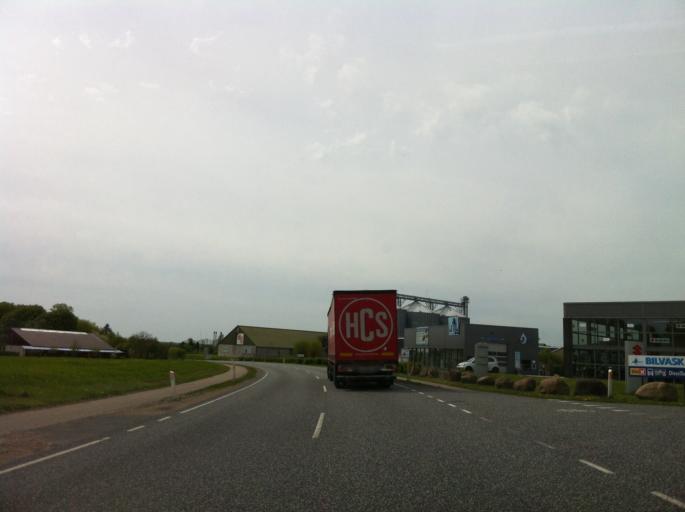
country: DK
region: Zealand
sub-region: Ringsted Kommune
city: Ringsted
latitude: 55.4351
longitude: 11.8149
